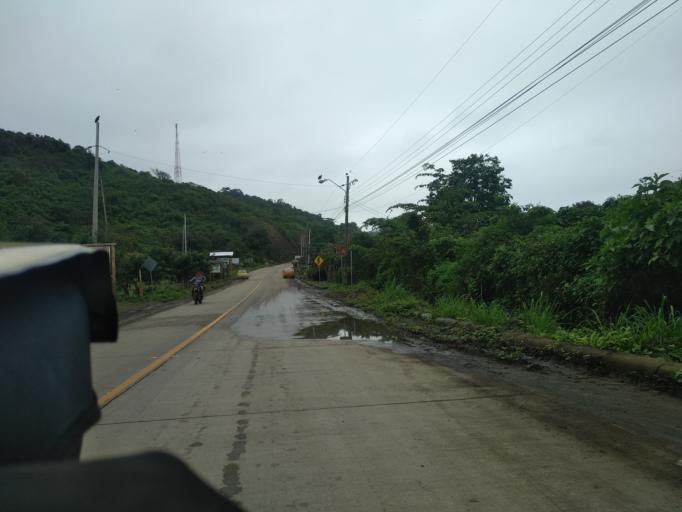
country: EC
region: Manabi
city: Pajan
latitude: -1.6760
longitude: -80.8111
